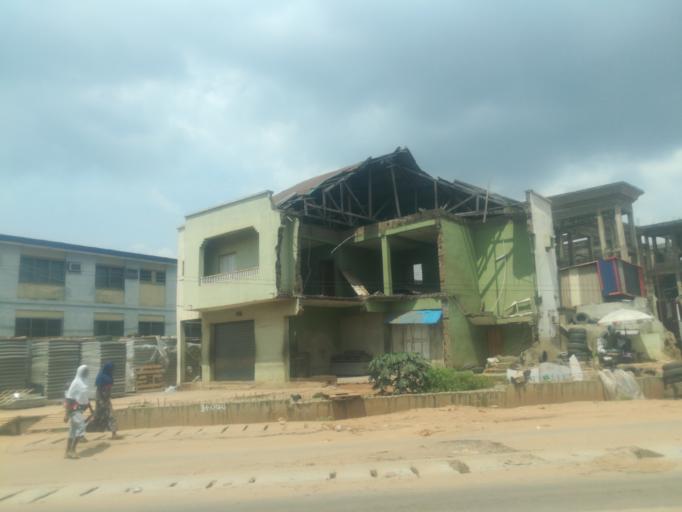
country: NG
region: Oyo
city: Ibadan
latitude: 7.4034
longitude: 3.9411
